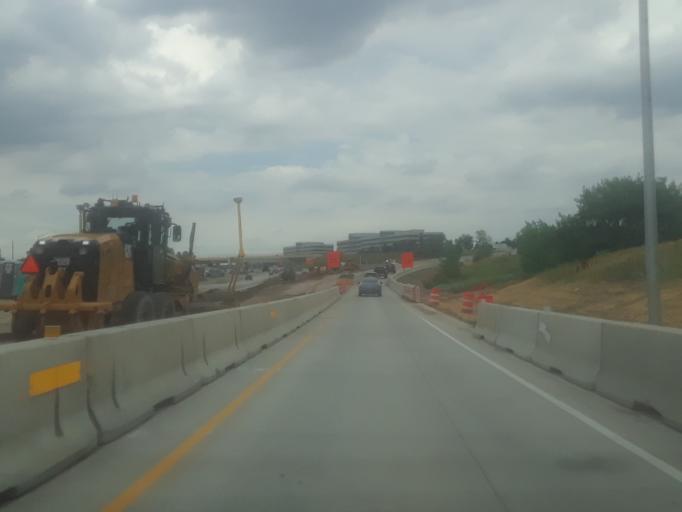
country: US
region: Colorado
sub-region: Arapahoe County
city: Columbine Valley
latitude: 39.5613
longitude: -105.0135
